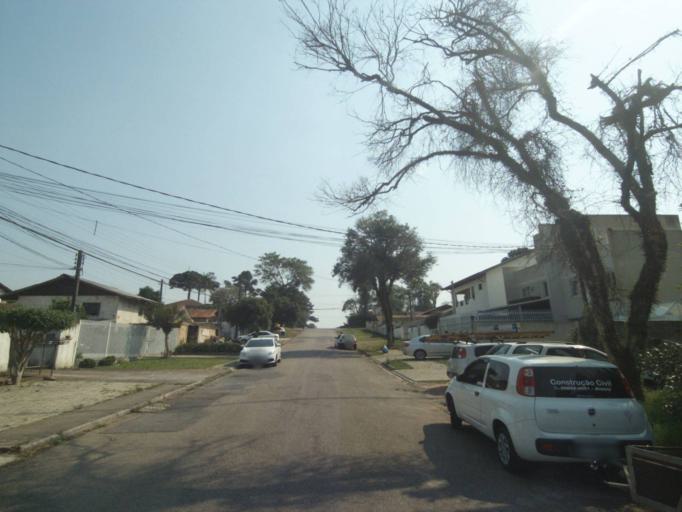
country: BR
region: Parana
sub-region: Sao Jose Dos Pinhais
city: Sao Jose dos Pinhais
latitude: -25.5233
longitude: -49.2538
